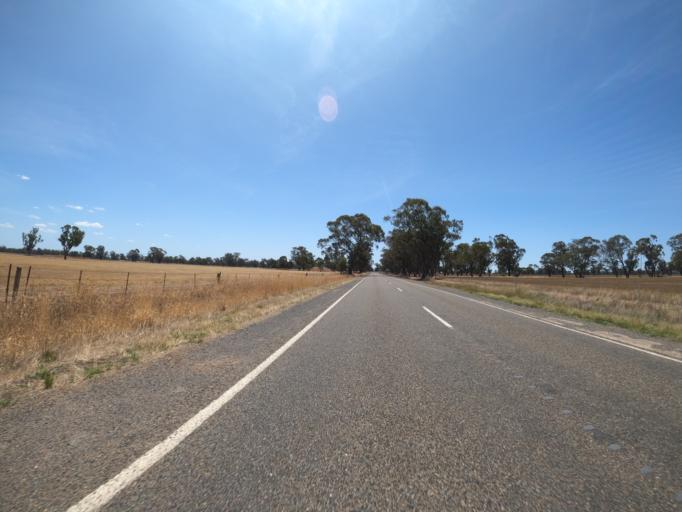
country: AU
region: Victoria
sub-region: Moira
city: Yarrawonga
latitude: -36.1852
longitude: 145.9672
